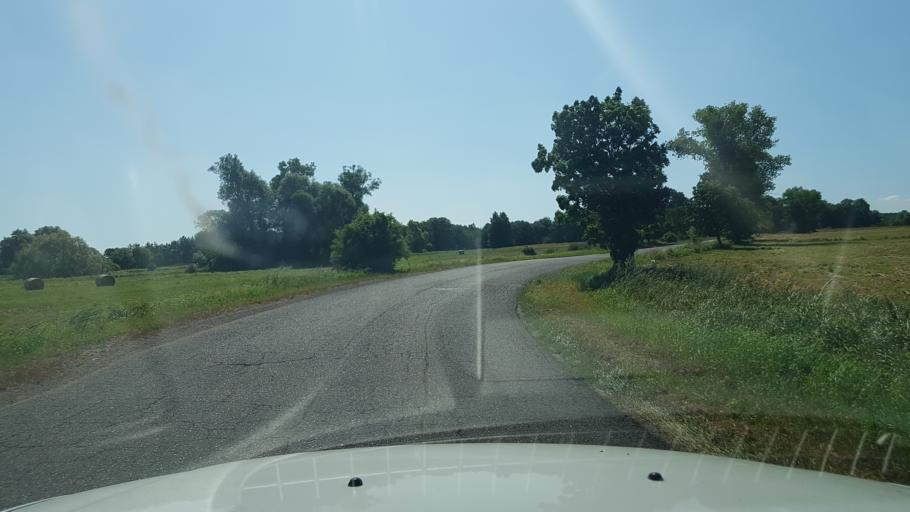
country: PL
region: West Pomeranian Voivodeship
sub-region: Powiat goleniowski
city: Goleniow
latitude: 53.4771
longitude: 14.7127
